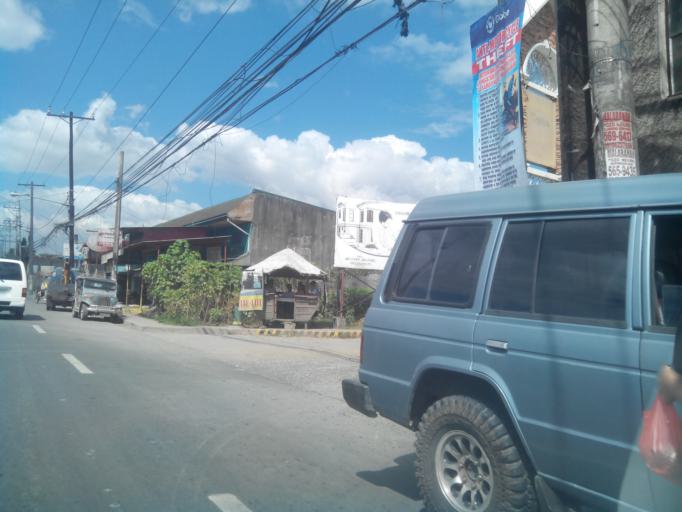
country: PH
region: Calabarzon
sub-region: Province of Rizal
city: Taytay
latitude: 14.5471
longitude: 121.1421
